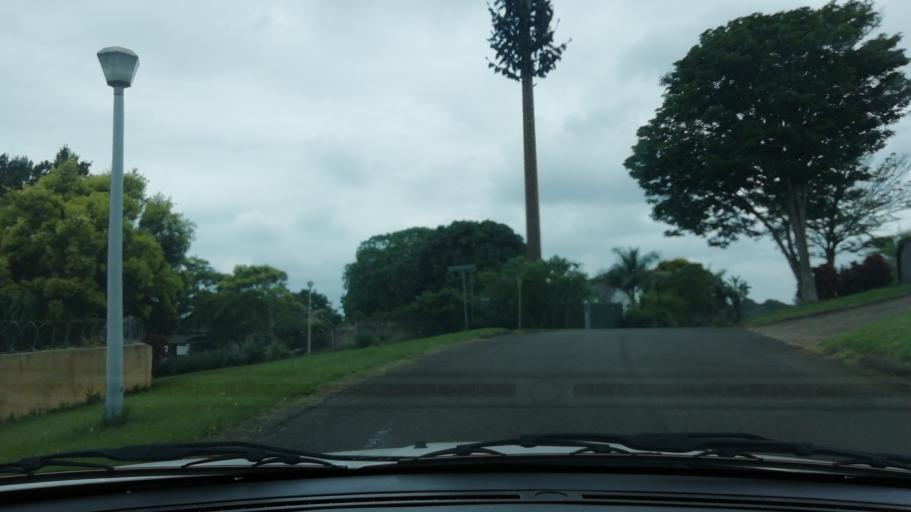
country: ZA
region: KwaZulu-Natal
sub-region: uThungulu District Municipality
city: Empangeni
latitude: -28.7592
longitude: 31.8881
